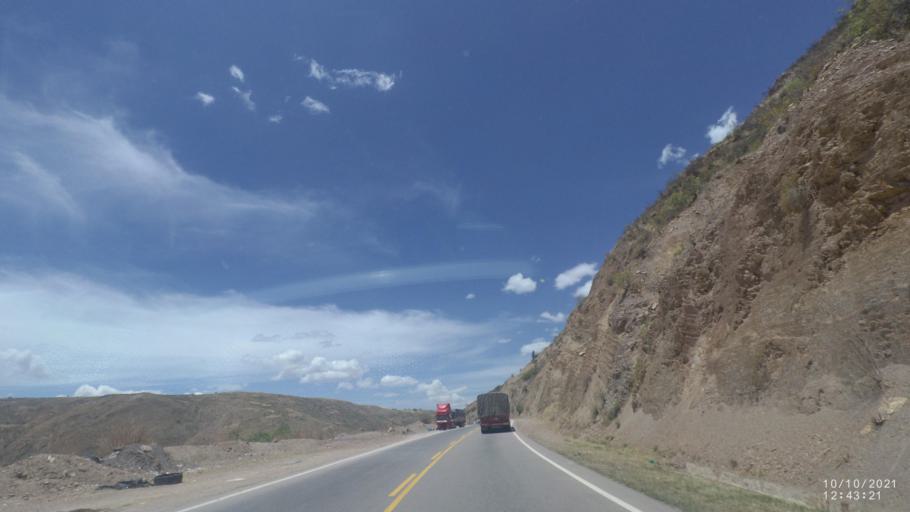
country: BO
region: Cochabamba
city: Irpa Irpa
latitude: -17.6300
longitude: -66.3858
